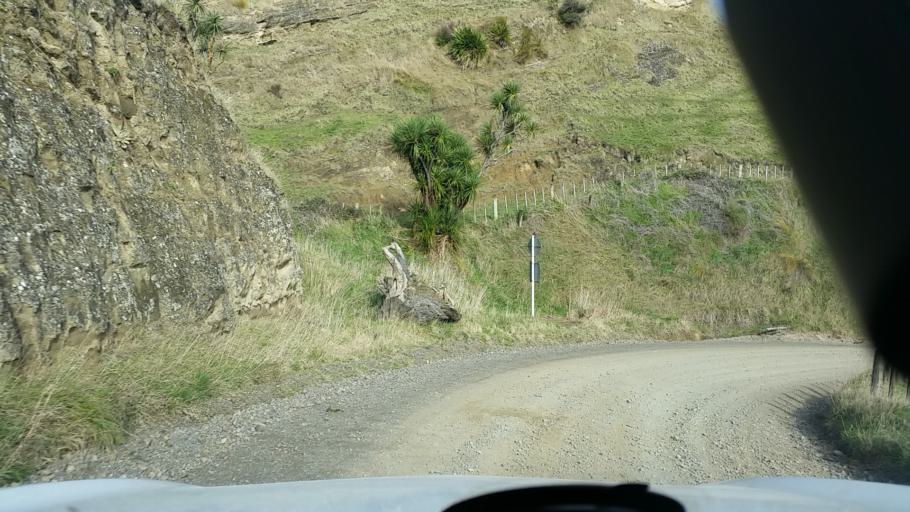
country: NZ
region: Hawke's Bay
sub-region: Napier City
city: Napier
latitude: -39.1111
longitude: 176.8952
